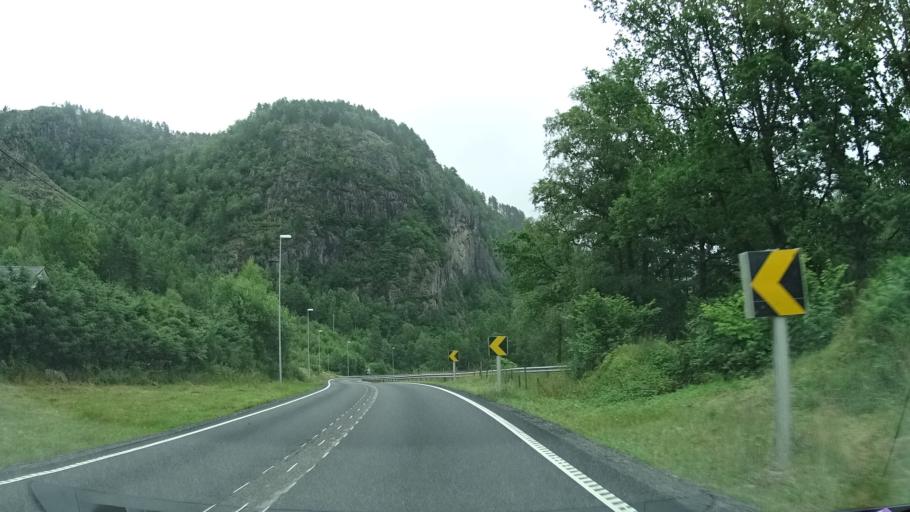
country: NO
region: Rogaland
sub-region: Lund
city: Moi
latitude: 58.4453
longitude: 6.5818
